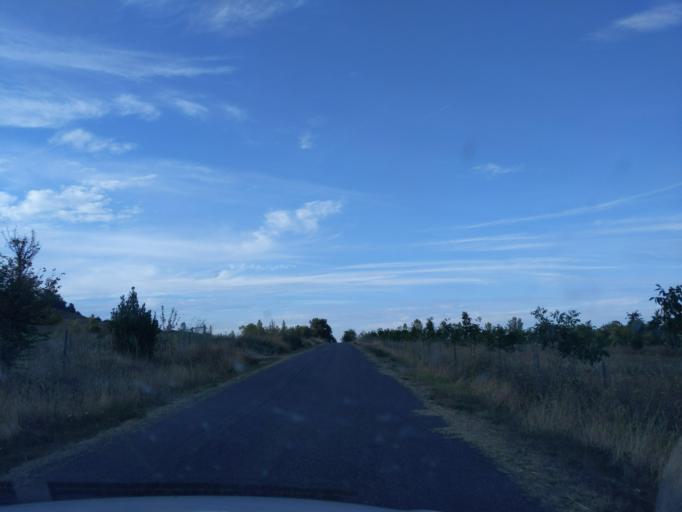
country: ES
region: La Rioja
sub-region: Provincia de La Rioja
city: Santurdejo
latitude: 42.3798
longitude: -2.9846
